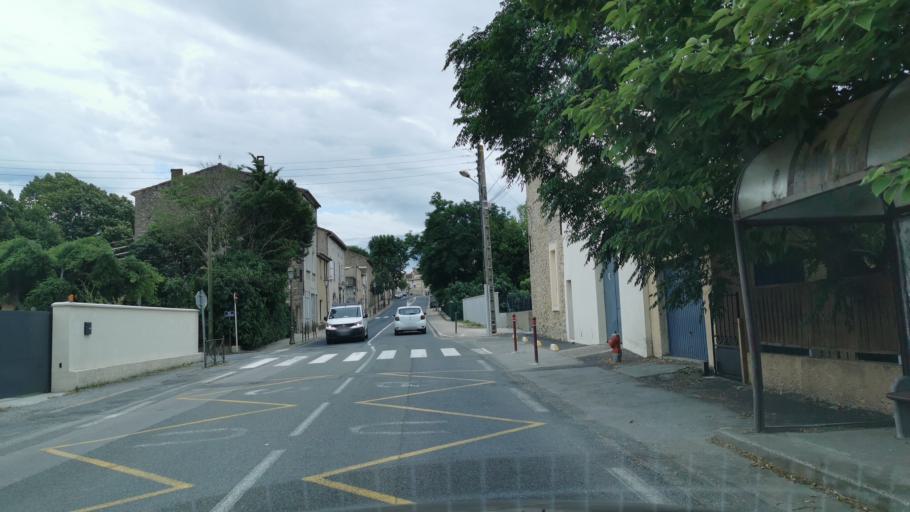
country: FR
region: Languedoc-Roussillon
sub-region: Departement de l'Aude
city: Marcorignan
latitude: 43.2282
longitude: 2.9229
